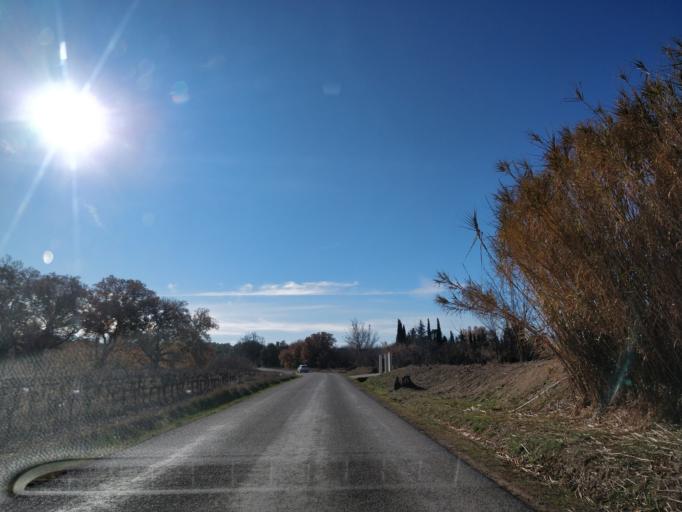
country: FR
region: Languedoc-Roussillon
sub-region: Departement de l'Herault
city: Beaulieu
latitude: 43.7666
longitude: 4.0194
